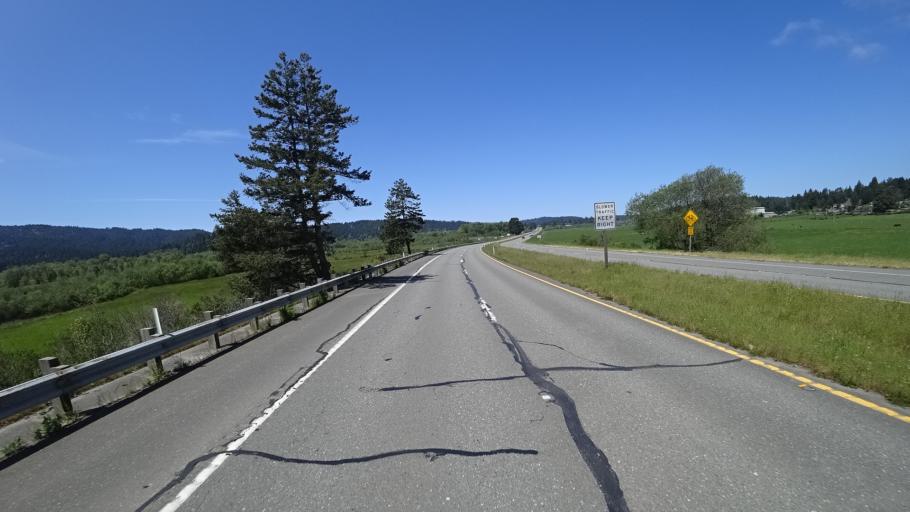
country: US
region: California
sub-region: Humboldt County
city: Blue Lake
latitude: 40.8889
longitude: -124.0030
